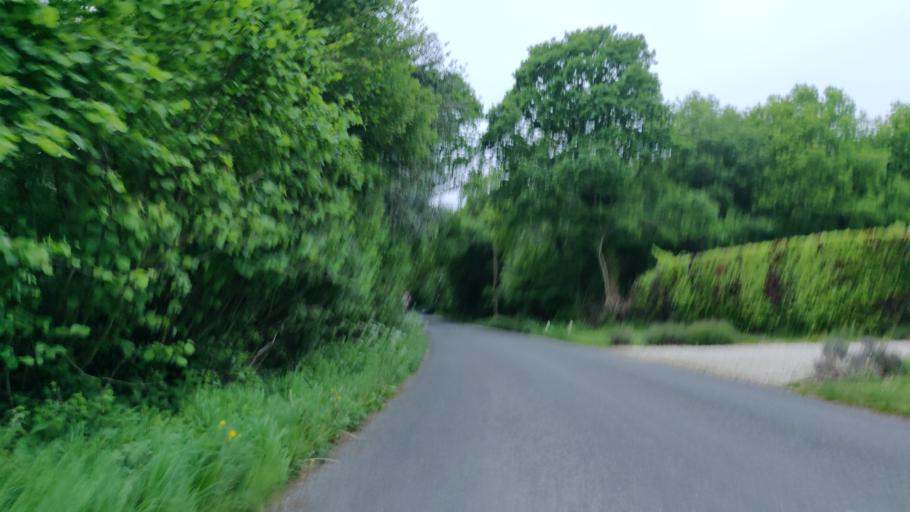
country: GB
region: England
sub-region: West Sussex
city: Southwater
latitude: 51.0388
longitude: -0.3359
